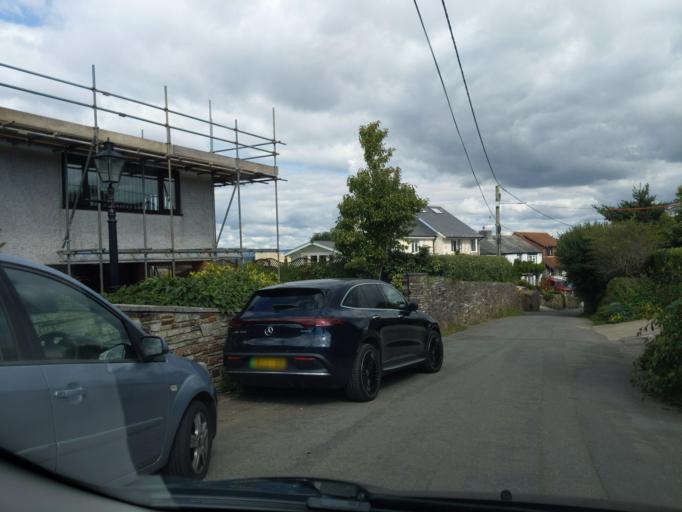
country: GB
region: England
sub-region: Plymouth
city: Plymstock
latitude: 50.3436
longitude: -4.0936
